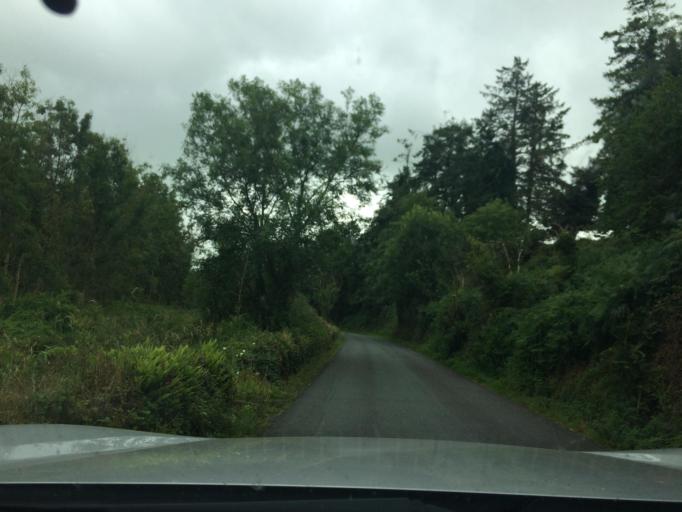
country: IE
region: Munster
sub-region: Waterford
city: Dungarvan
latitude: 52.1934
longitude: -7.7294
